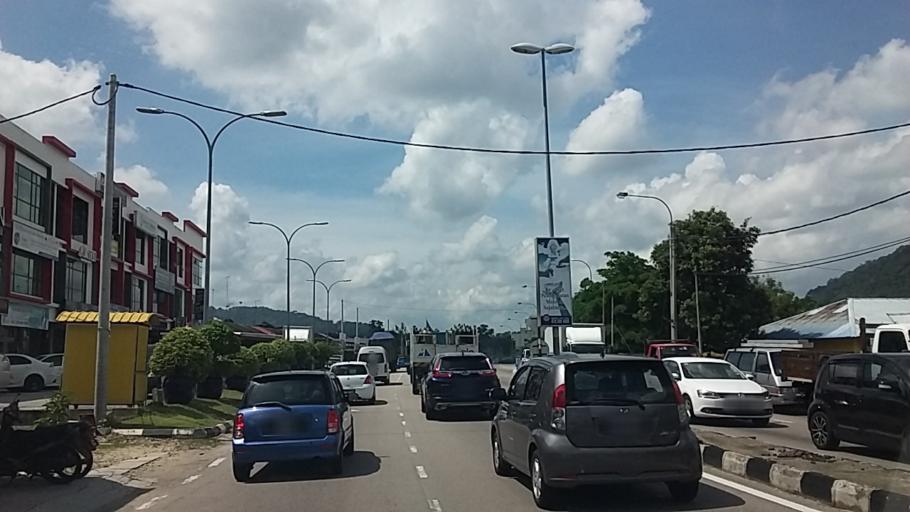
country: MY
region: Johor
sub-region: Daerah Batu Pahat
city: Batu Pahat
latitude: 1.8451
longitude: 102.9412
